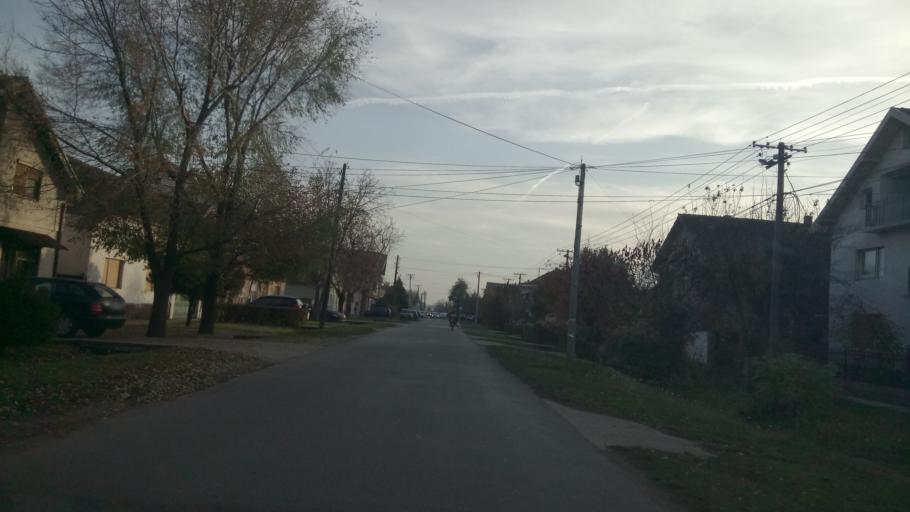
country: RS
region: Autonomna Pokrajina Vojvodina
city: Nova Pazova
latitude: 44.9401
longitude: 20.2157
